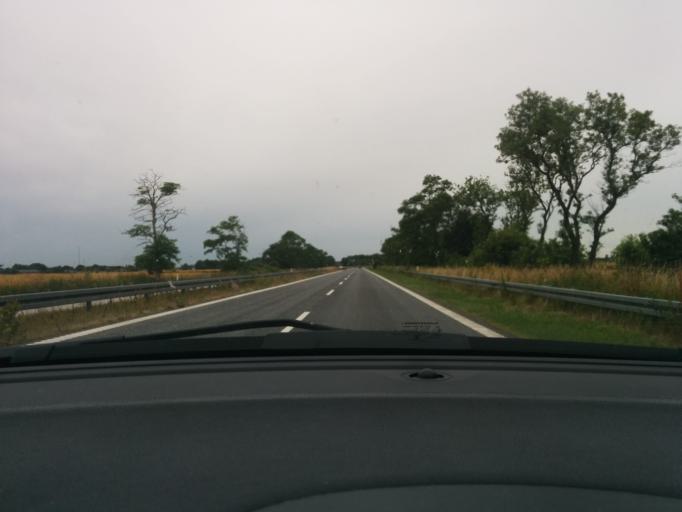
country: DK
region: Zealand
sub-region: Lolland Kommune
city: Maribo
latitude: 54.7913
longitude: 11.5381
